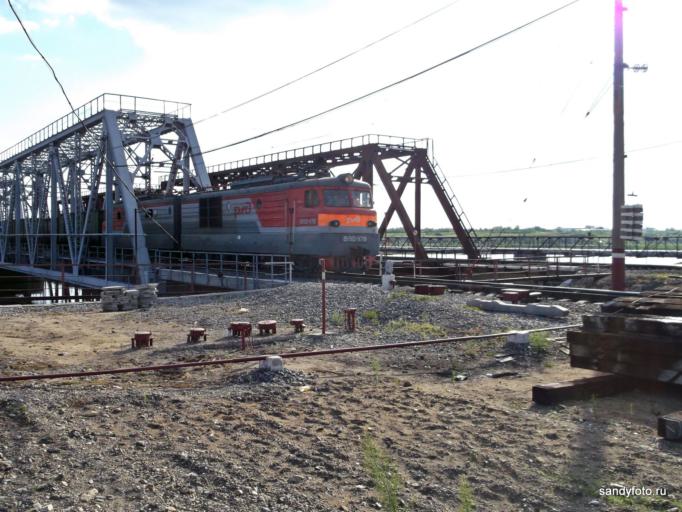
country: RU
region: Chelyabinsk
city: Troitsk
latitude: 54.0563
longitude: 61.6125
